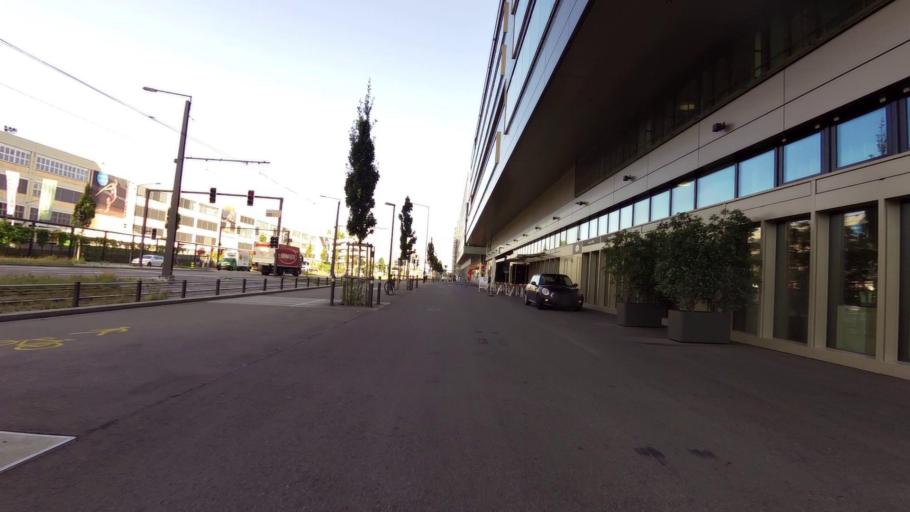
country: CH
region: Zurich
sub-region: Bezirk Zuerich
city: Zuerich (Kreis 5) / Escher-Wyss
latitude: 47.3907
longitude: 8.5093
